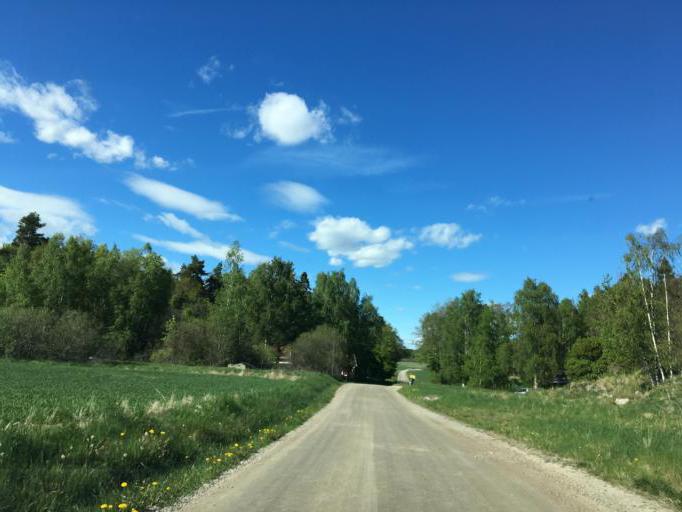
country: SE
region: Soedermanland
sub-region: Eskilstuna Kommun
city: Kvicksund
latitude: 59.3987
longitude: 16.2379
